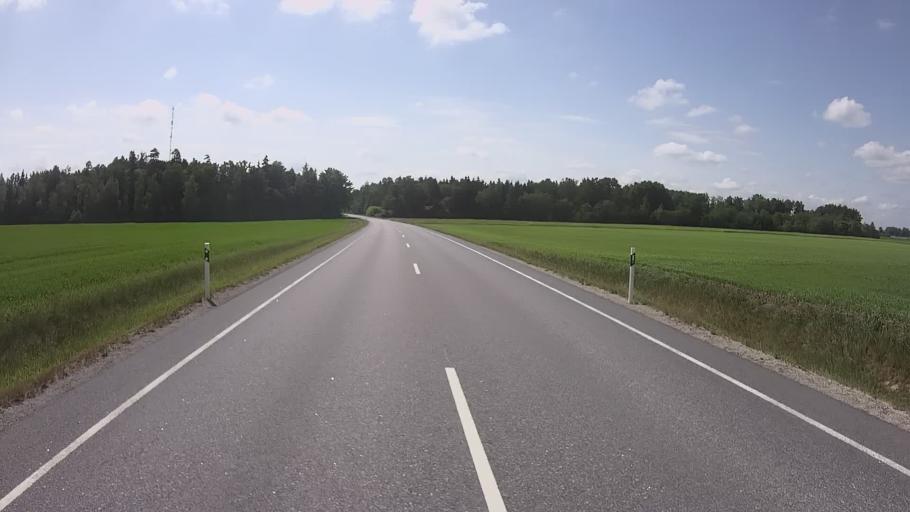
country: EE
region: Tartu
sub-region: Tartu linn
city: Tartu
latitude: 58.3757
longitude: 26.8840
